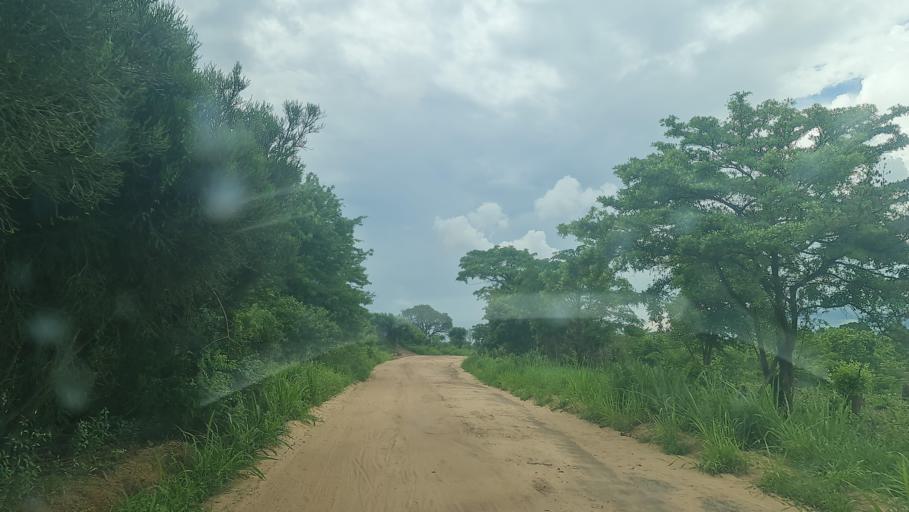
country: MW
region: Southern Region
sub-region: Nsanje District
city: Nsanje
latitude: -17.5869
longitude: 35.6684
